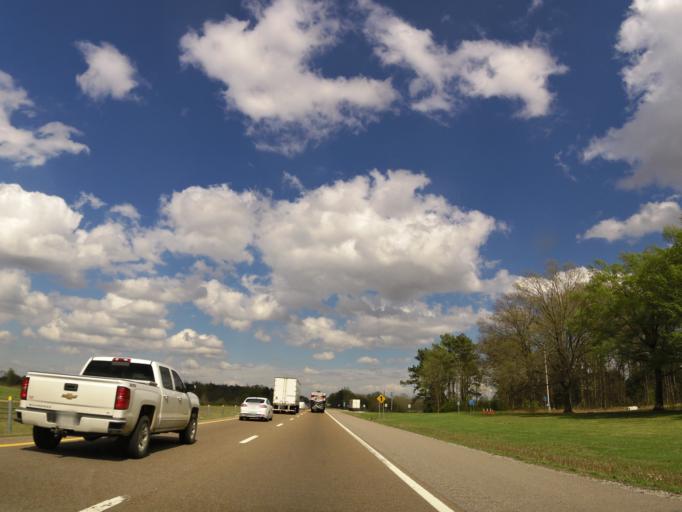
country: US
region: Tennessee
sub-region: Crockett County
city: Bells
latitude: 35.6243
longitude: -88.9767
